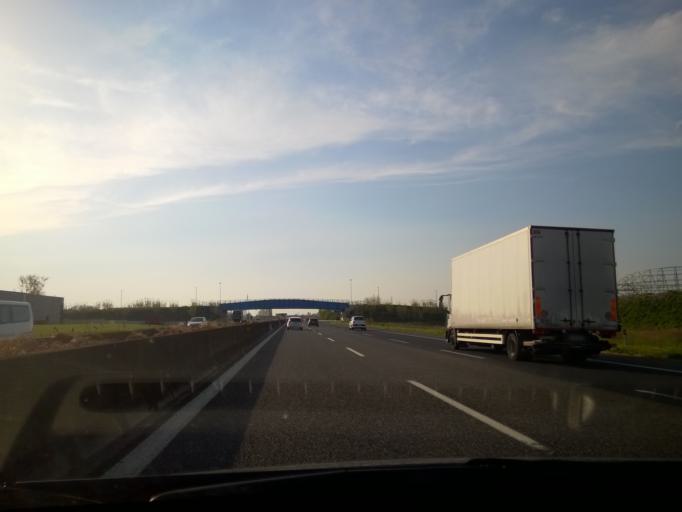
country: IT
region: Emilia-Romagna
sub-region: Provincia di Ravenna
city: Faenza
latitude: 44.3275
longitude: 11.8957
